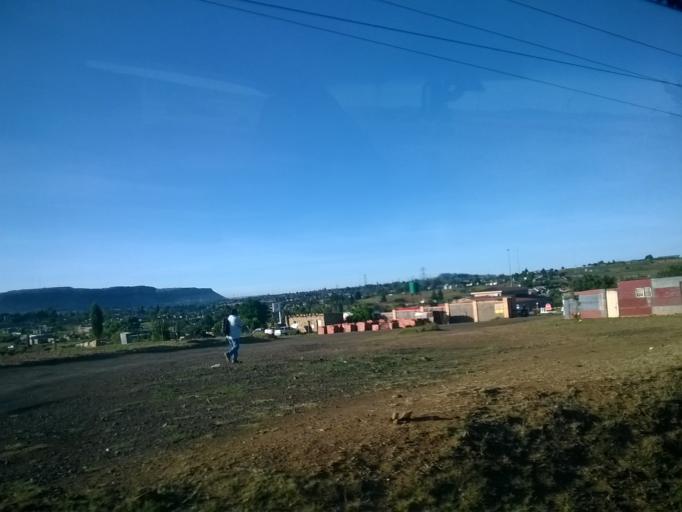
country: LS
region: Maseru
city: Maseru
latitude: -29.2649
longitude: 27.5531
